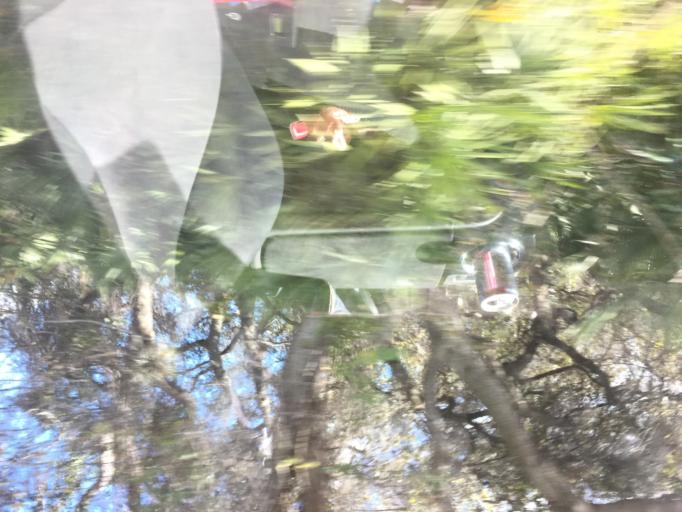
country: US
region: Florida
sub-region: Pinellas County
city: Saint George
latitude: 28.0470
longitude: -82.7428
